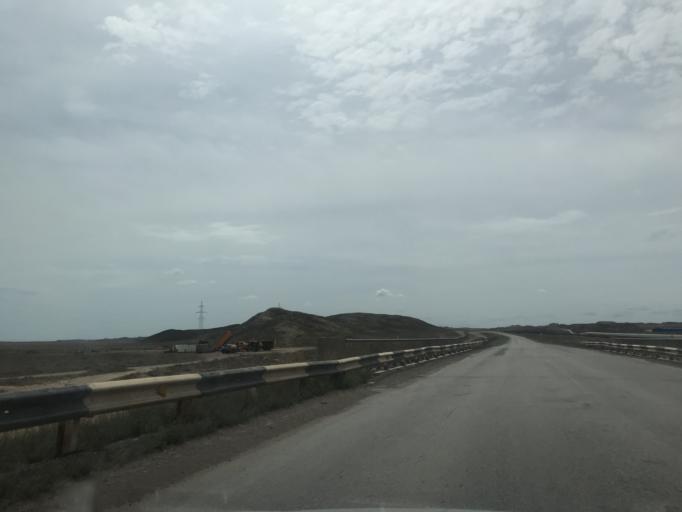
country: KZ
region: Zhambyl
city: Mynaral
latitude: 45.3746
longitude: 73.6560
